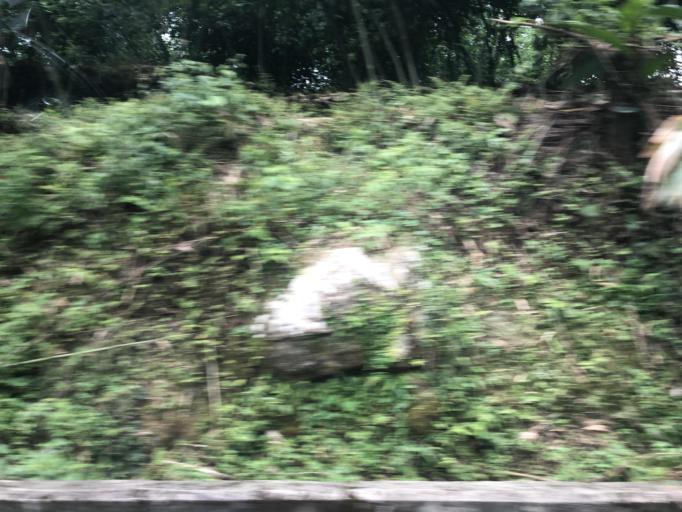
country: TW
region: Taiwan
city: Daxi
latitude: 24.8779
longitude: 121.4166
